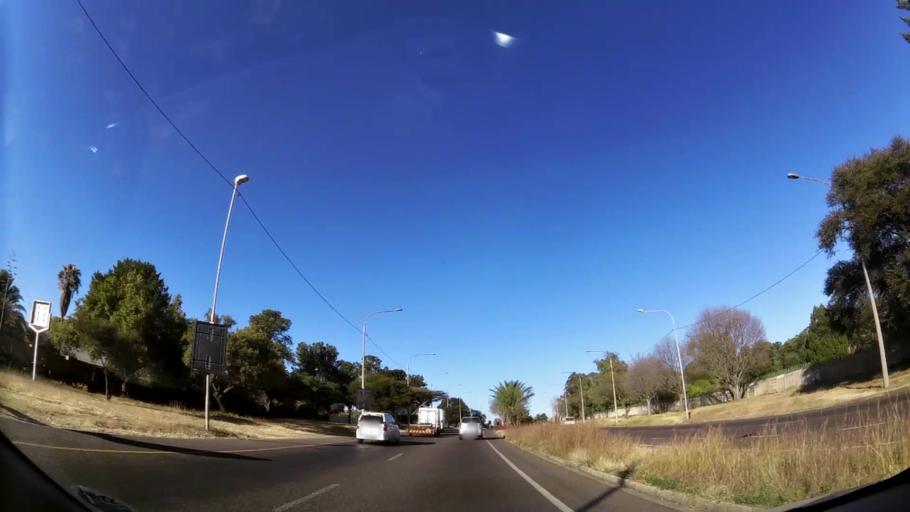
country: ZA
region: Gauteng
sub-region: West Rand District Municipality
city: Krugersdorp
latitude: -26.0830
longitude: 27.7894
